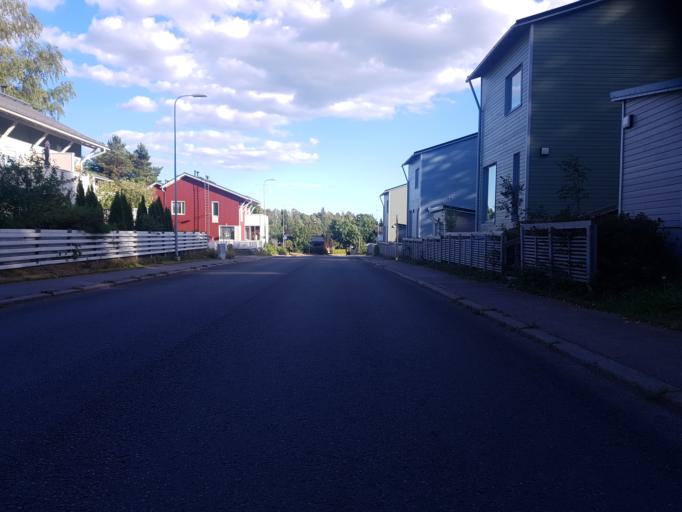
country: FI
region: Uusimaa
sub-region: Helsinki
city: Vantaa
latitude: 60.2587
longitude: 24.9804
